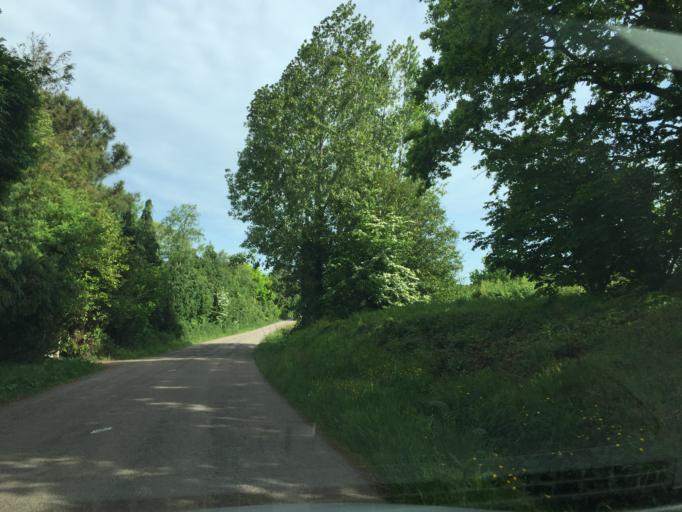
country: FR
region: Brittany
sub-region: Departement des Cotes-d'Armor
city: Matignon
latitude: 48.6432
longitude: -2.3246
